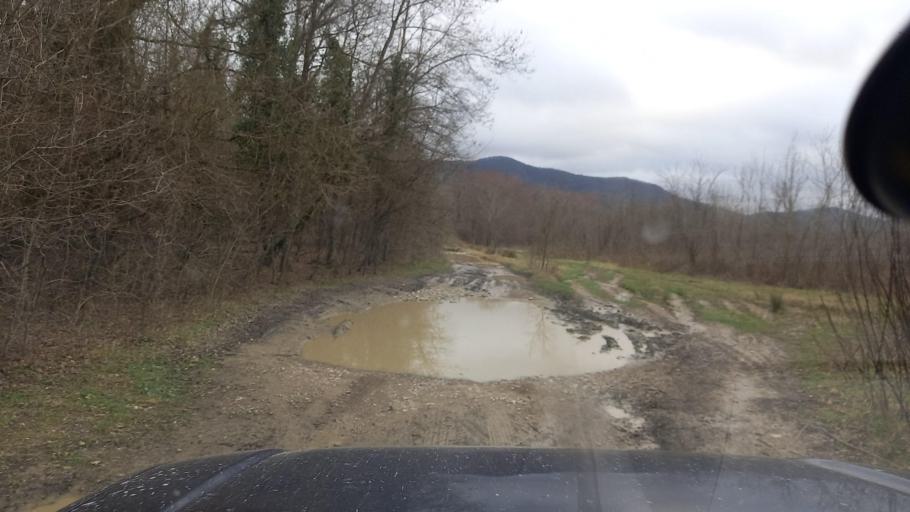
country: RU
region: Krasnodarskiy
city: Pshada
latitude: 44.4919
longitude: 38.4118
